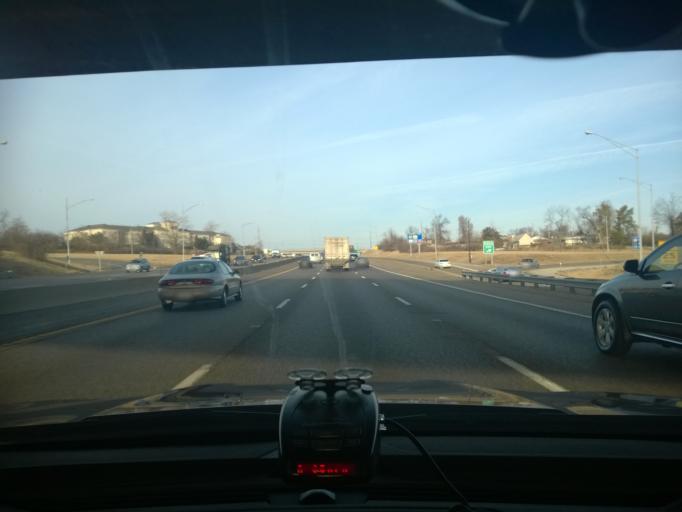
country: US
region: Missouri
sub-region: Saint Louis County
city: Saint Ann
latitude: 38.7438
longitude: -90.3963
